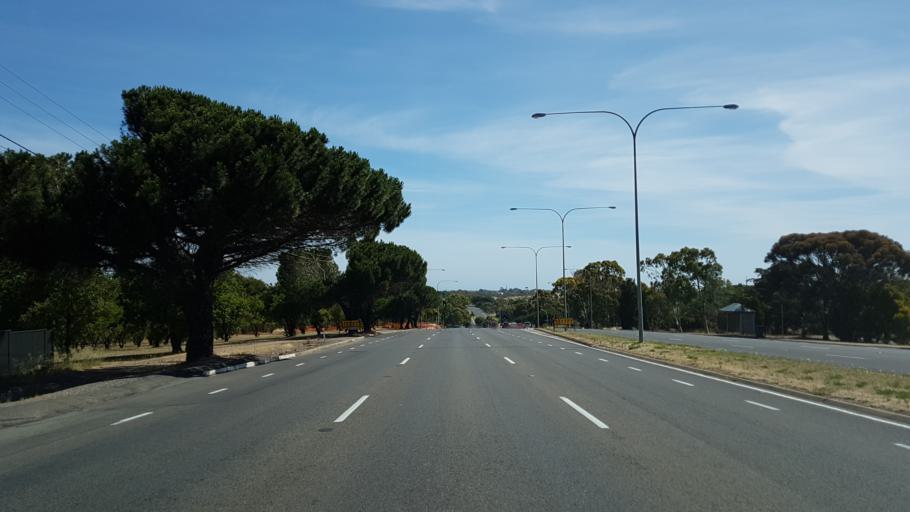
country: AU
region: South Australia
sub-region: Marion
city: Trott Park
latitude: -35.0741
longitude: 138.5517
